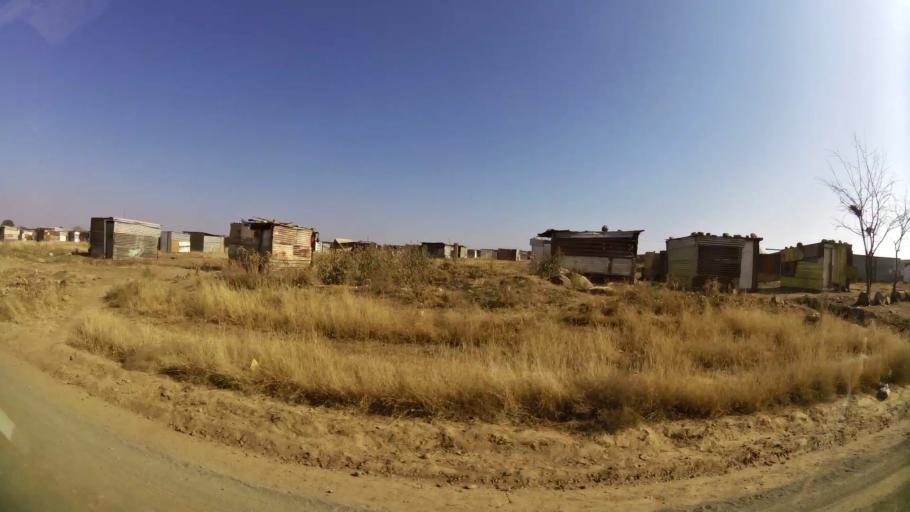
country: ZA
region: Orange Free State
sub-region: Mangaung Metropolitan Municipality
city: Bloemfontein
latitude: -29.1867
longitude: 26.2851
